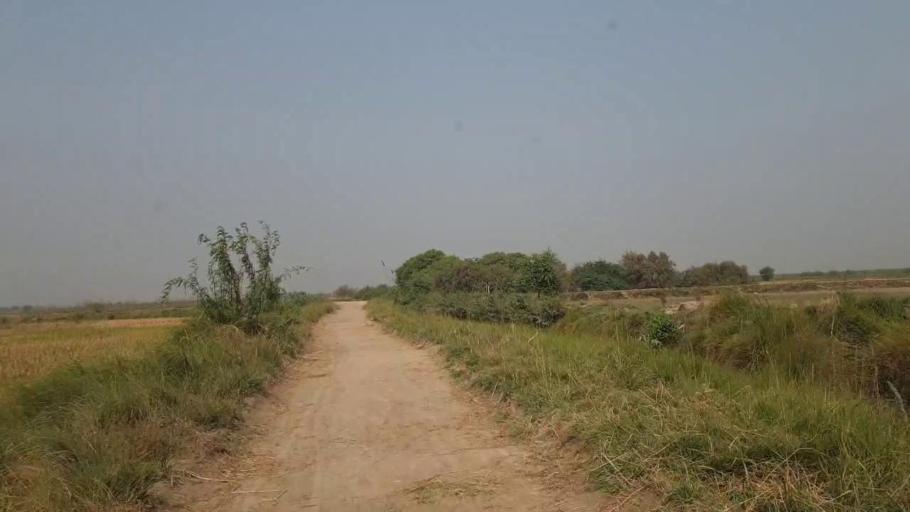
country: PK
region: Sindh
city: Matli
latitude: 25.1223
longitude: 68.6534
